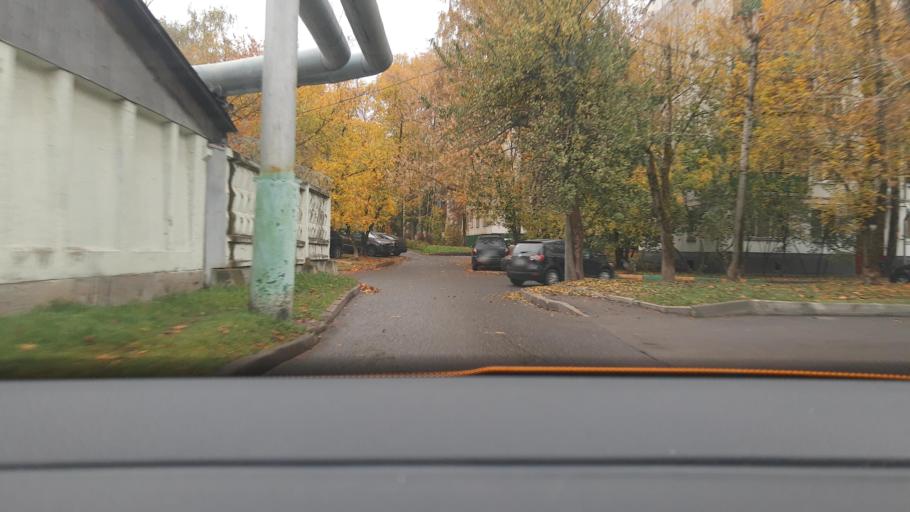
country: RU
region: Moscow
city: Metrogorodok
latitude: 55.8264
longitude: 37.7583
